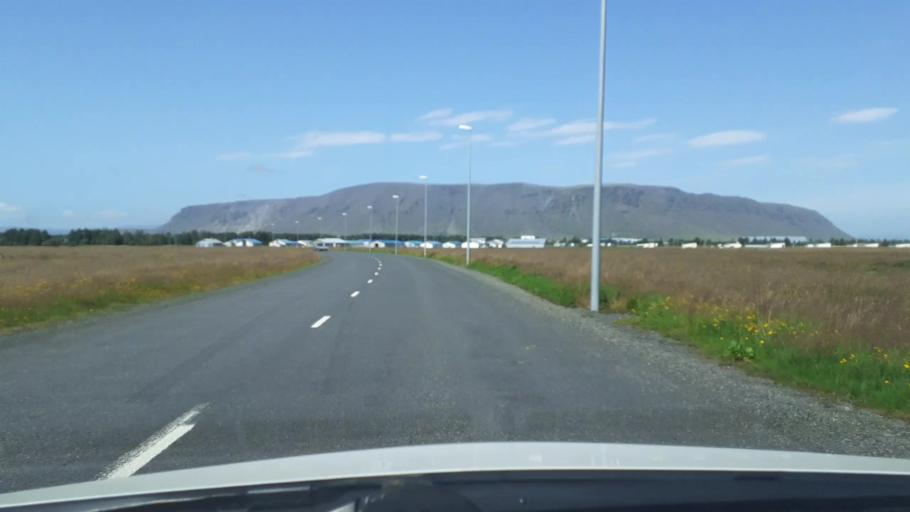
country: IS
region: South
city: Selfoss
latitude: 63.9284
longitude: -20.9694
